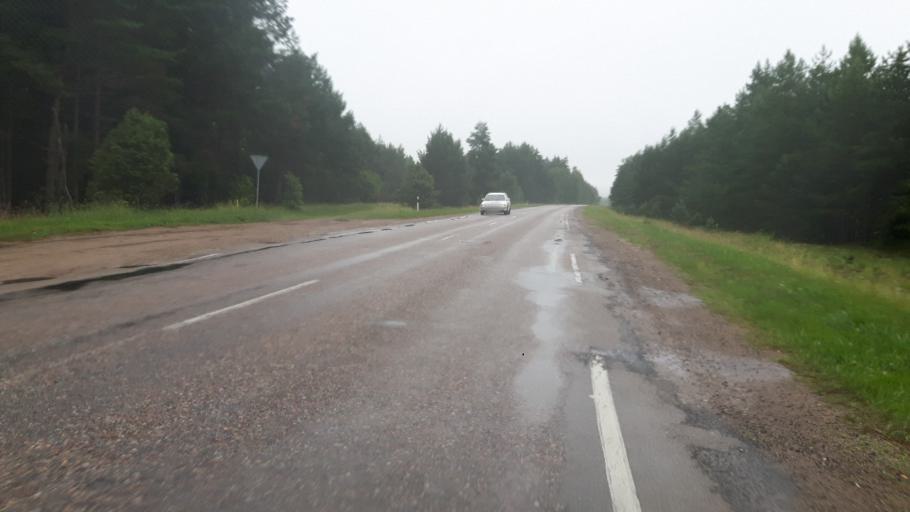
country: LT
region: Klaipedos apskritis
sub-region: Palanga
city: Sventoji
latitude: 56.0880
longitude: 21.1251
